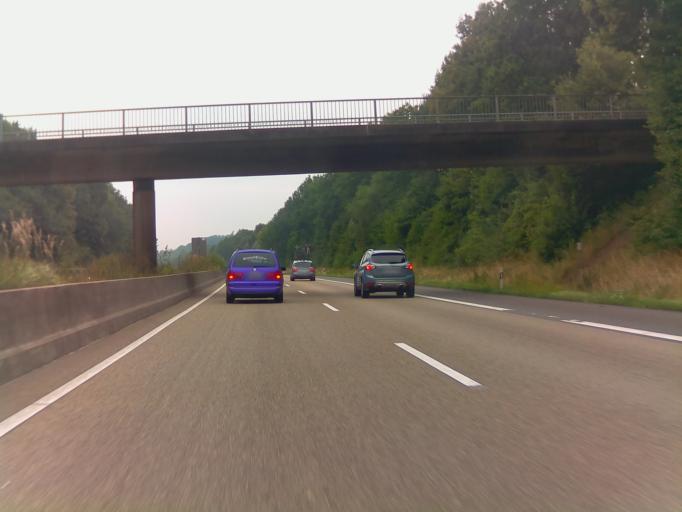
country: DE
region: Hesse
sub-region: Regierungsbezirk Kassel
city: Niederaula
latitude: 50.7504
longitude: 9.6271
